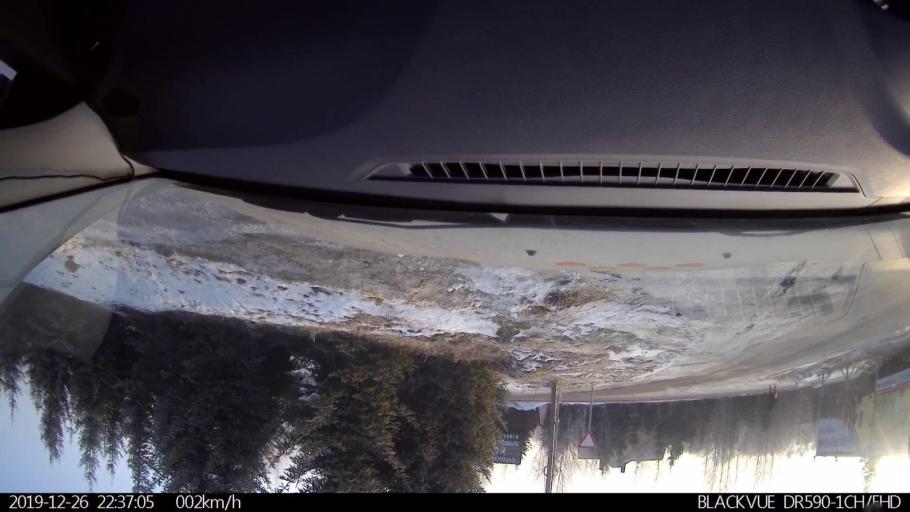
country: RU
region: Nizjnij Novgorod
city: Burevestnik
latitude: 56.1461
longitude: 43.7219
